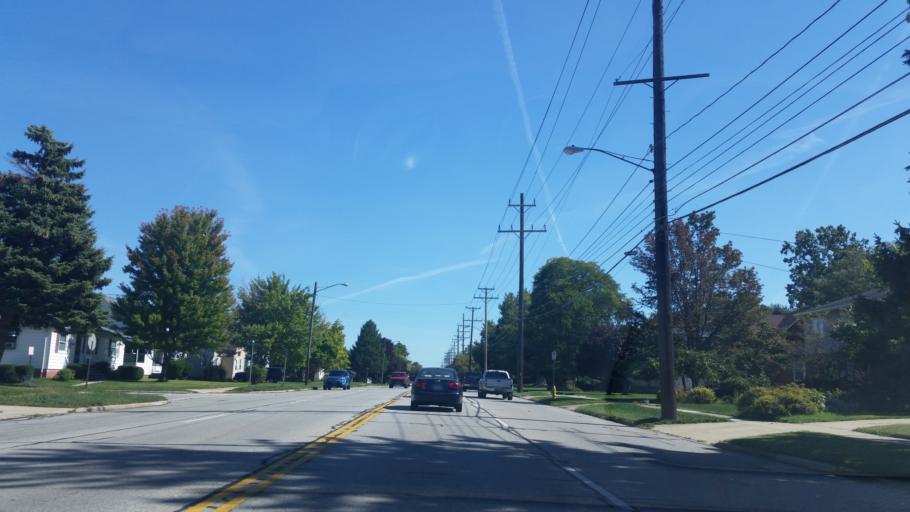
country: US
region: Ohio
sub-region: Cuyahoga County
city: Parma
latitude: 41.4049
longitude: -81.7177
